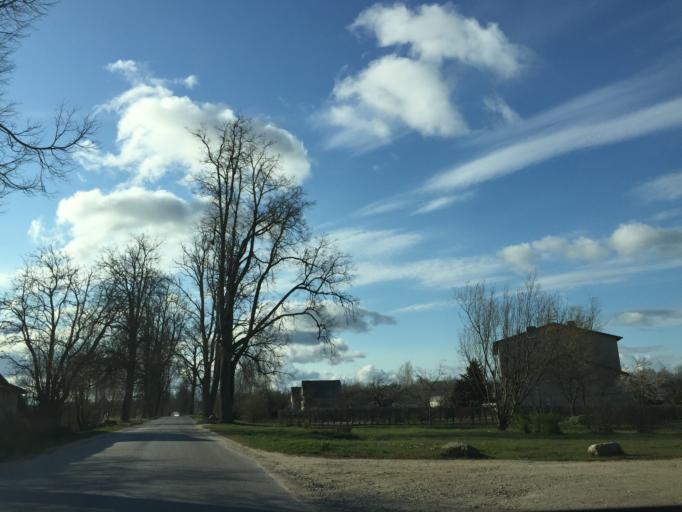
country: LV
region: Burtnieki
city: Matisi
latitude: 57.5980
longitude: 25.0934
